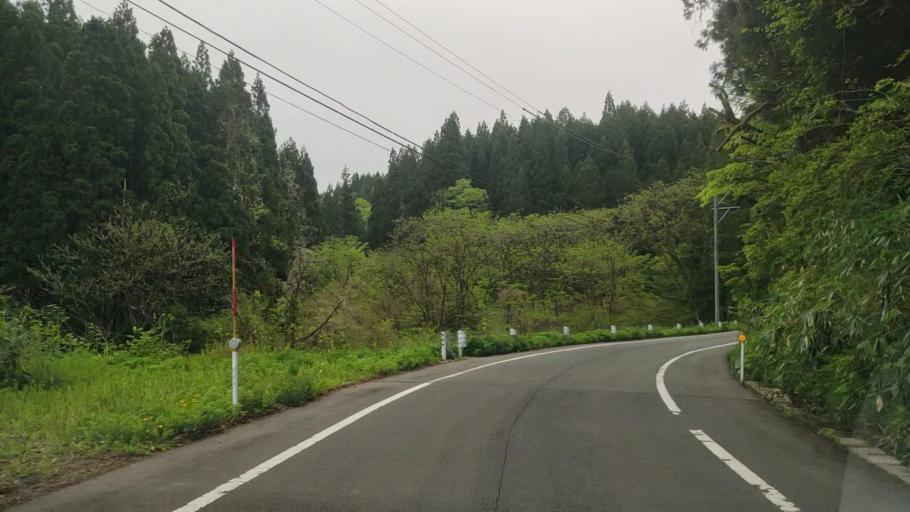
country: JP
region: Niigata
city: Gosen
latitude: 37.7143
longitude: 139.1233
